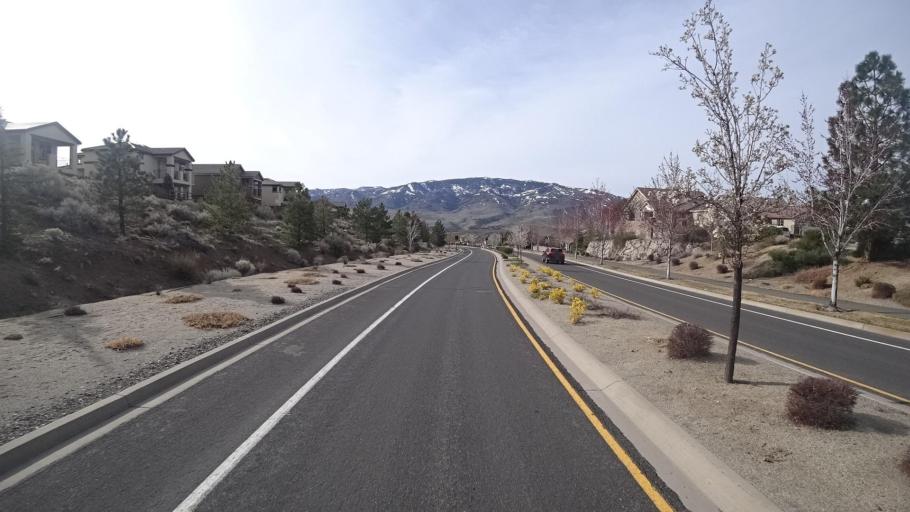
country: US
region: Nevada
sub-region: Washoe County
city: Mogul
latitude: 39.5295
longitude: -119.9492
